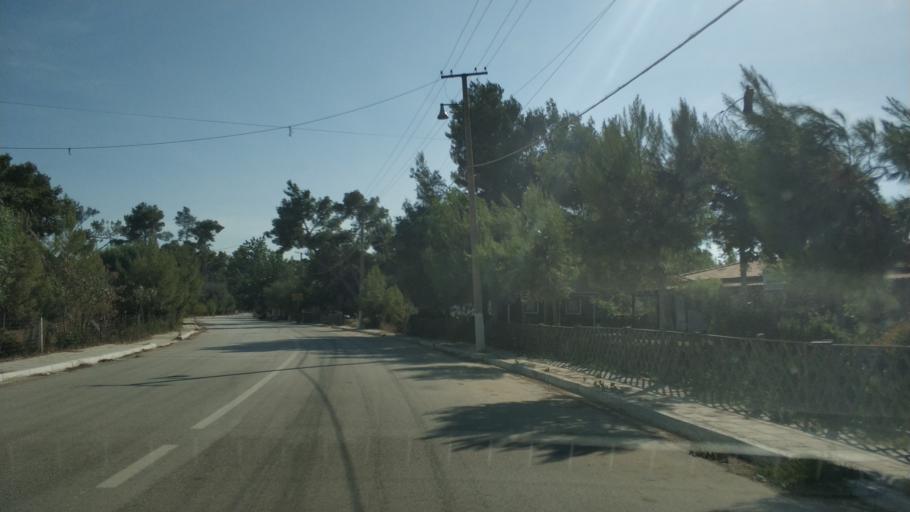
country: AL
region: Fier
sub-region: Rrethi i Lushnjes
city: Divjake
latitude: 40.9687
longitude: 19.4788
